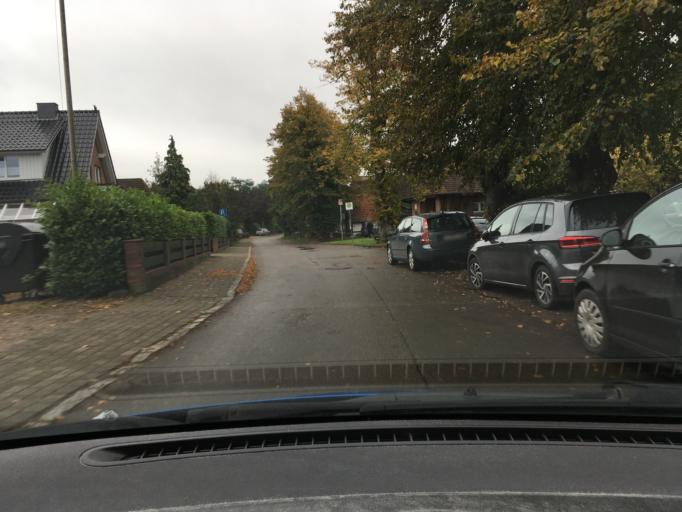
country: DE
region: Schleswig-Holstein
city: Bosau
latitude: 54.1053
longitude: 10.4281
